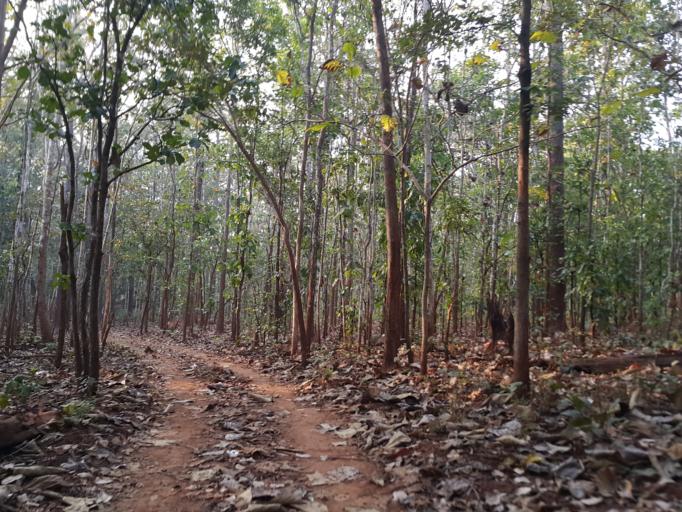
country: TH
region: Lamphun
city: Li
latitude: 17.6172
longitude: 98.8986
